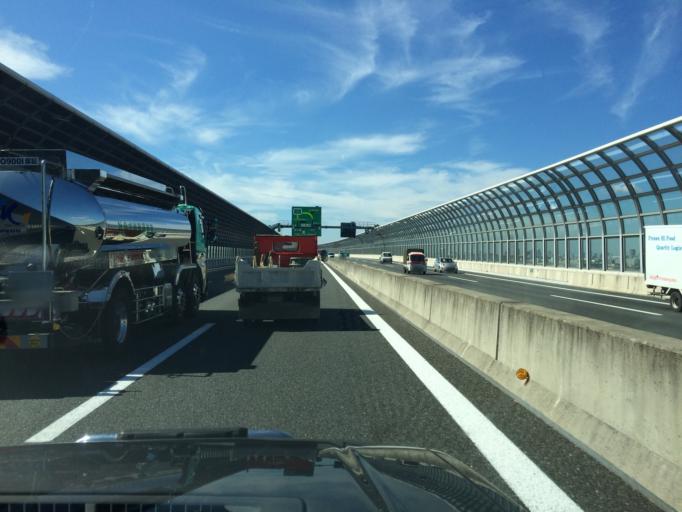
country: JP
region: Osaka
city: Daitocho
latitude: 34.7317
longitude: 135.6069
